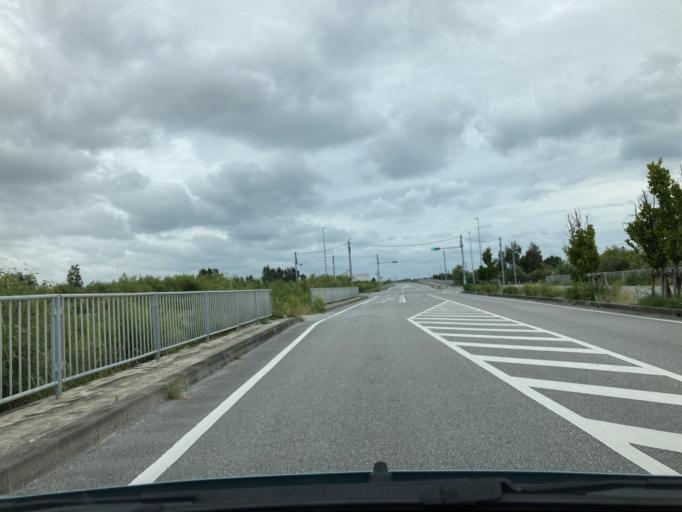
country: JP
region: Okinawa
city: Ginowan
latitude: 26.2126
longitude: 127.7679
